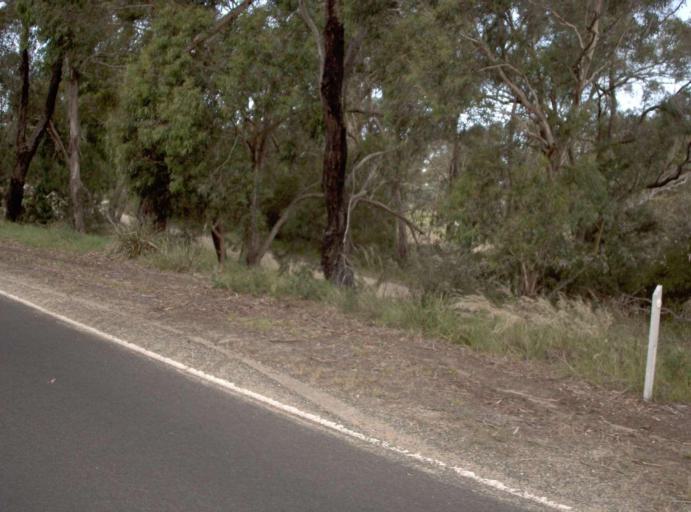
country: AU
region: Victoria
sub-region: Wellington
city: Sale
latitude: -38.2176
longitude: 147.1179
